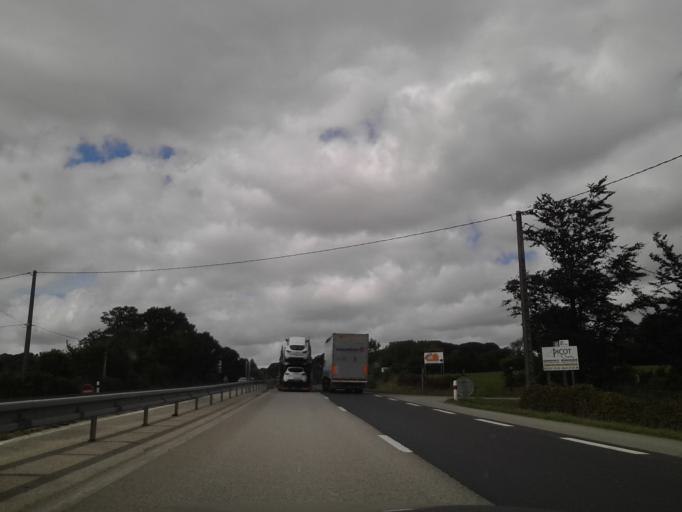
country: FR
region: Lower Normandy
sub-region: Departement de la Manche
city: Valognes
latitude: 49.5283
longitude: -1.5159
